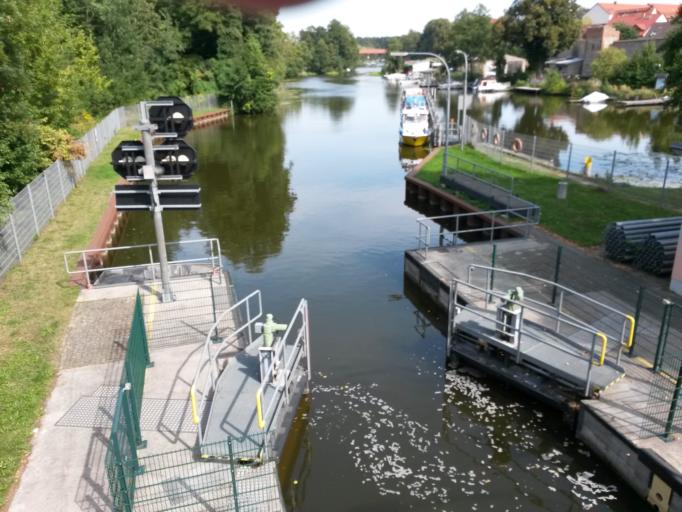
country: DE
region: Brandenburg
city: Templin
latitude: 53.1225
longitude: 13.4951
